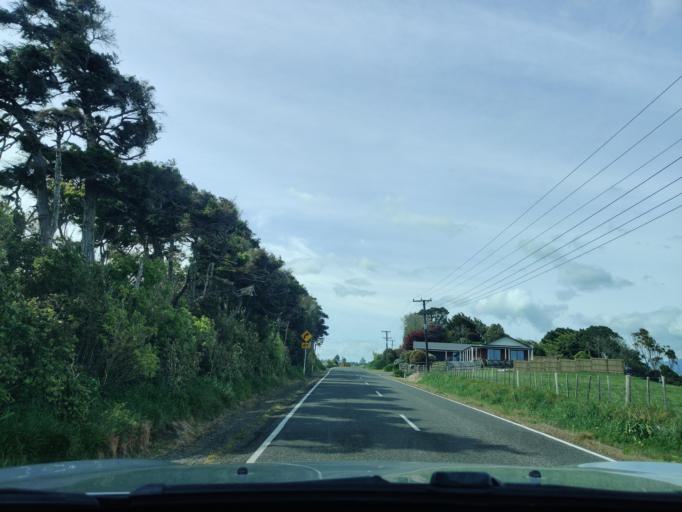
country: NZ
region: Taranaki
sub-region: New Plymouth District
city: New Plymouth
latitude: -39.1088
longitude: 174.1000
